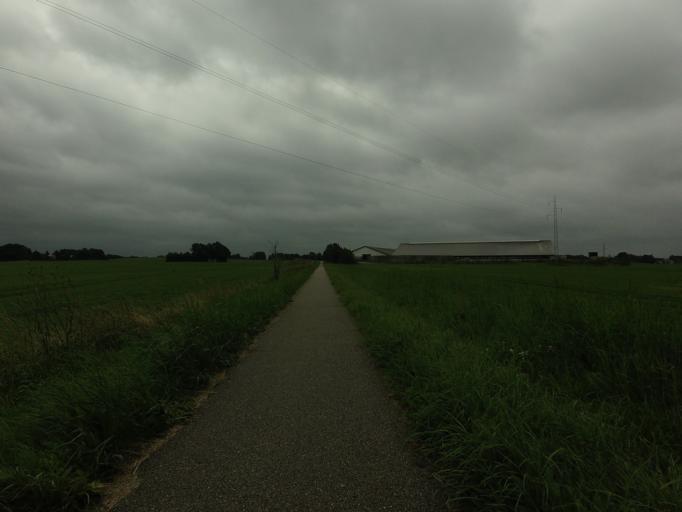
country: DK
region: Central Jutland
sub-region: Horsens Kommune
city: Braedstrup
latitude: 55.9866
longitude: 9.5922
